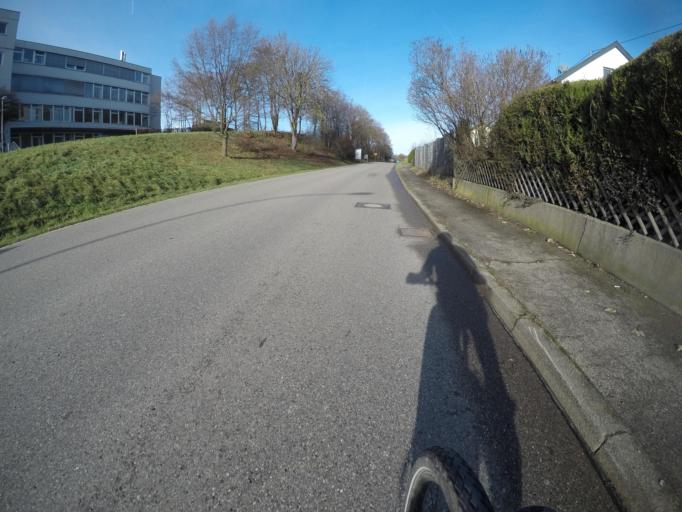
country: DE
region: Baden-Wuerttemberg
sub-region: Regierungsbezirk Stuttgart
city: Korb
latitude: 48.8466
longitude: 9.3570
